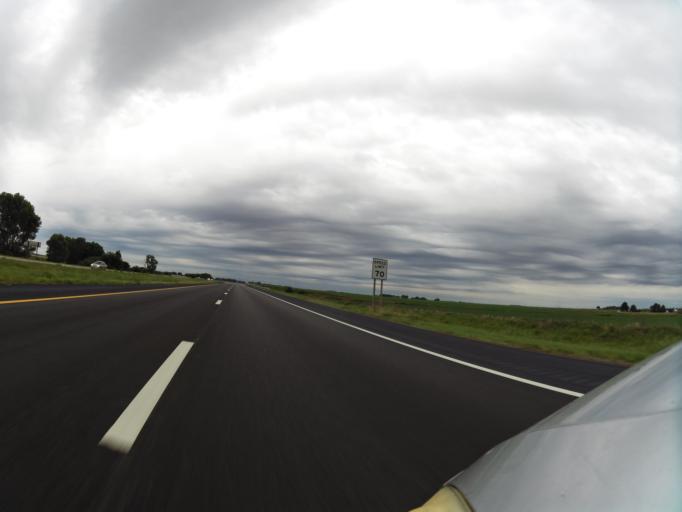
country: US
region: Kansas
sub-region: Sedgwick County
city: Colwich
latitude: 37.8385
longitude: -97.5719
